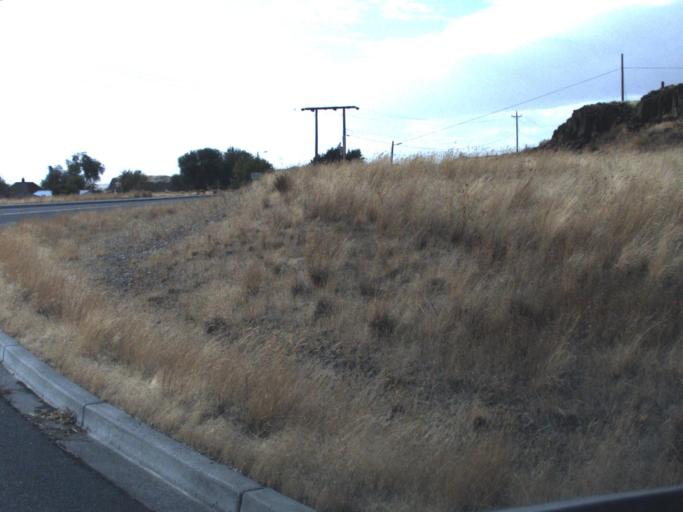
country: US
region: Washington
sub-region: Adams County
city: Ritzville
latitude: 47.3380
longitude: -118.6890
